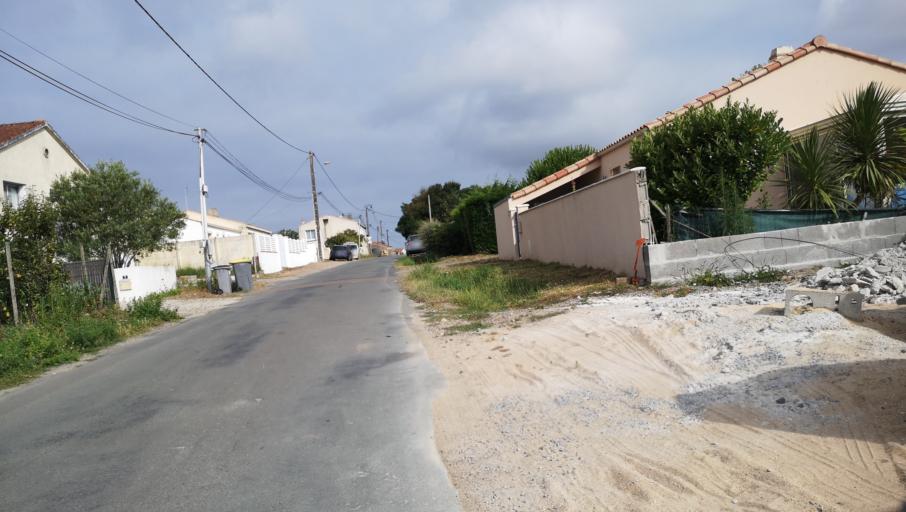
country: FR
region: Pays de la Loire
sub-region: Departement de la Vendee
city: Olonne-sur-Mer
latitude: 46.5487
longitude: -1.8002
